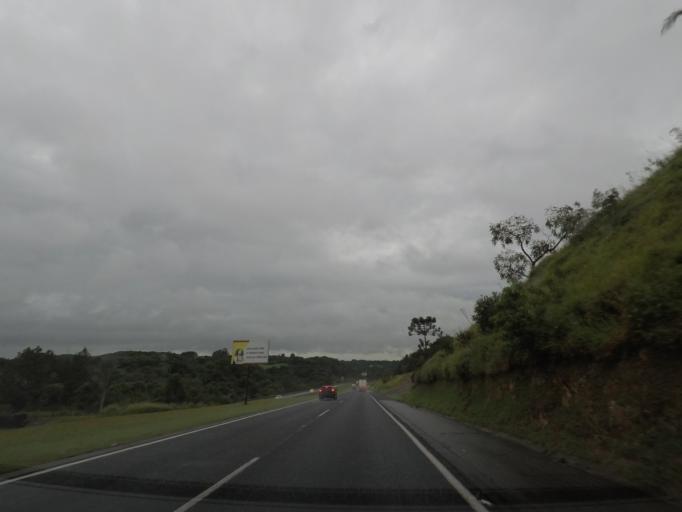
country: BR
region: Parana
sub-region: Curitiba
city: Curitiba
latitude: -25.4314
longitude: -49.3987
